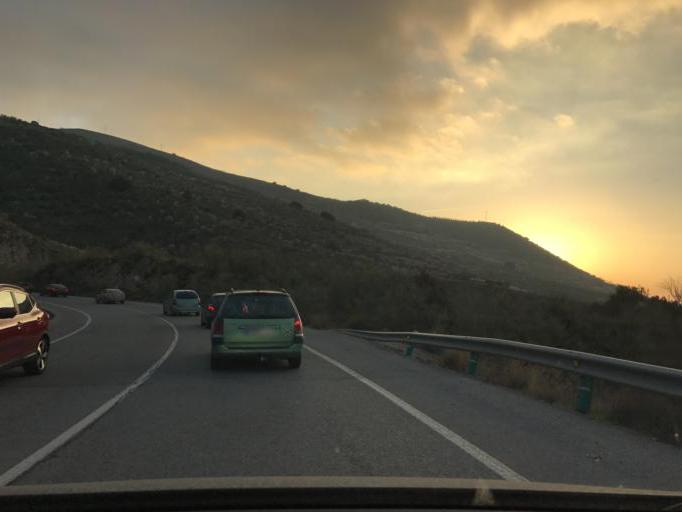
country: ES
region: Andalusia
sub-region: Provincia de Granada
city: Pinos Genil
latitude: 37.1544
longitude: -3.4981
